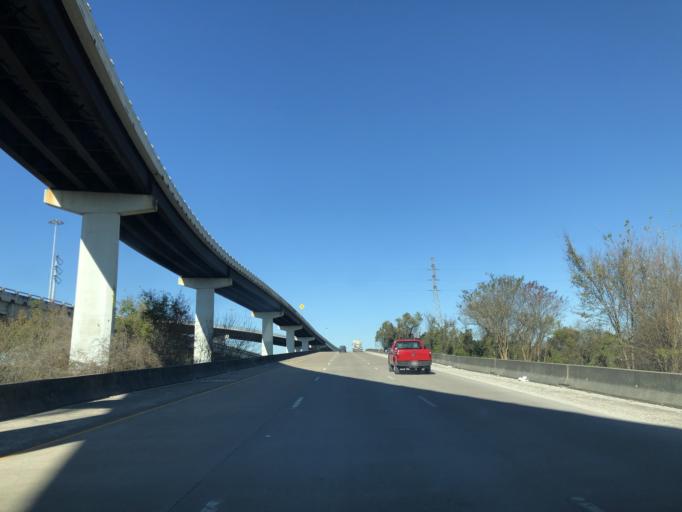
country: US
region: Texas
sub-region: Harris County
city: Cloverleaf
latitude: 29.7723
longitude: -95.1538
